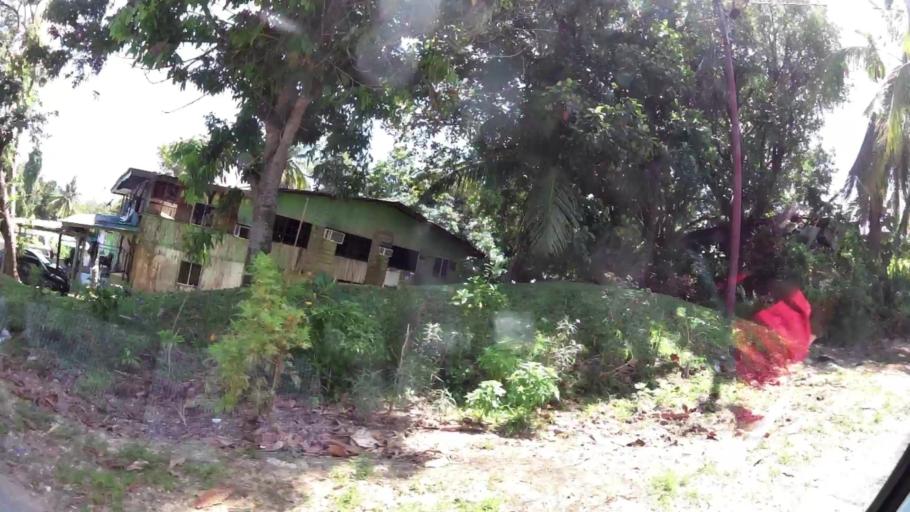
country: BN
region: Brunei and Muara
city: Bandar Seri Begawan
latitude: 4.9322
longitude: 114.9533
